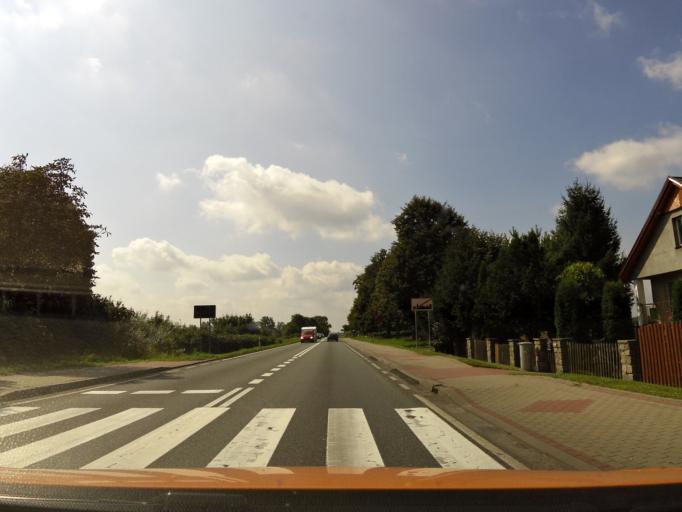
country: PL
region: West Pomeranian Voivodeship
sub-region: Powiat goleniowski
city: Nowogard
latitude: 53.7166
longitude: 15.1878
